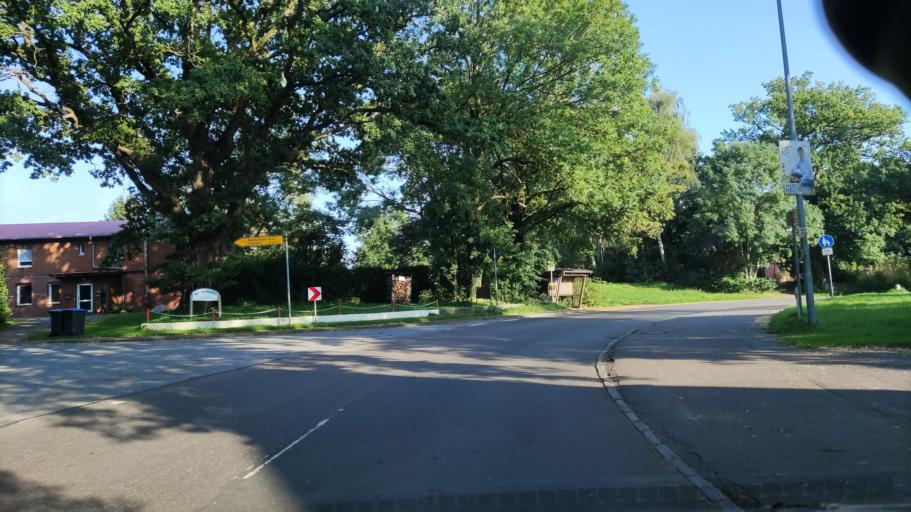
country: DE
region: Schleswig-Holstein
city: Willenscharen
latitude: 54.0100
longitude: 9.8087
